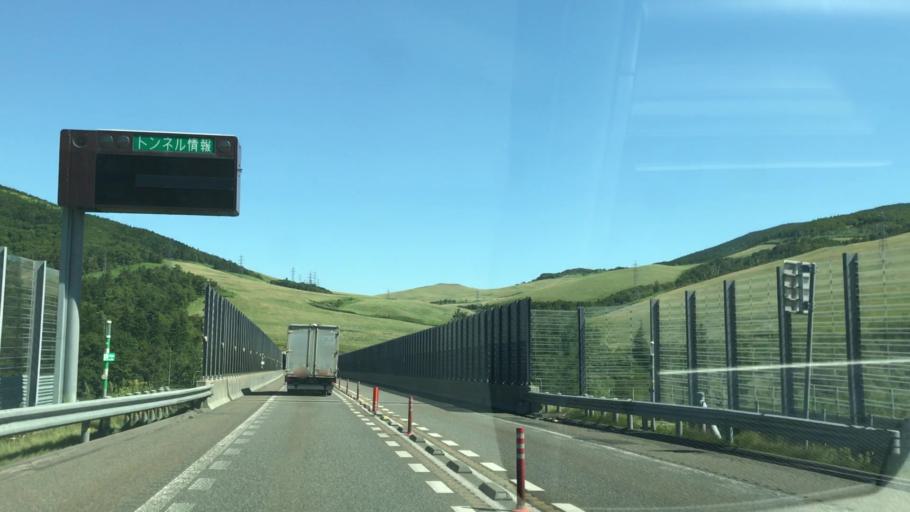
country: JP
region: Hokkaido
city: Shimo-furano
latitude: 43.0598
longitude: 142.7142
